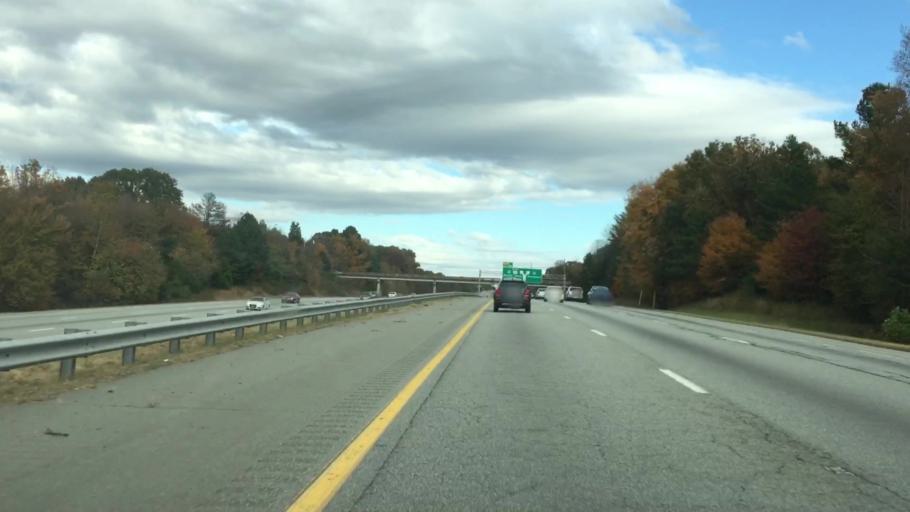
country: US
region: North Carolina
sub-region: Forsyth County
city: Clemmons
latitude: 36.0503
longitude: -80.3611
